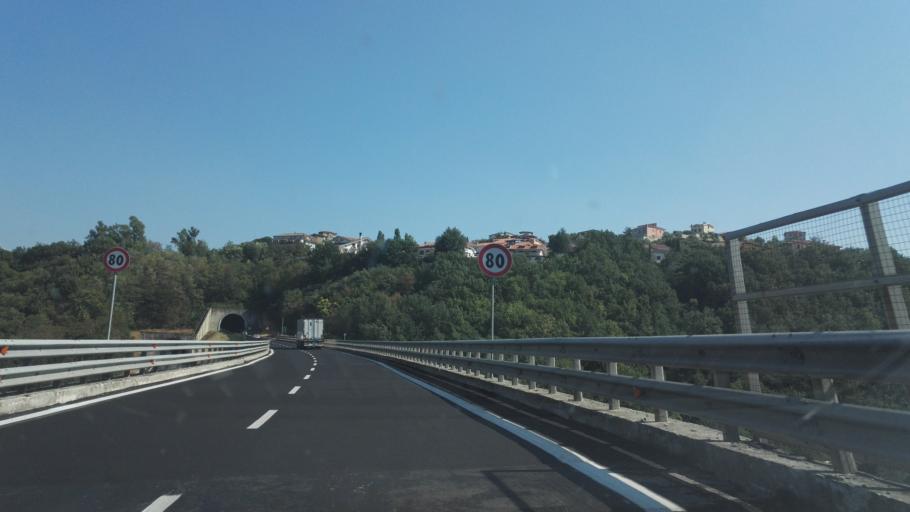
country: IT
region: Calabria
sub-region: Provincia di Cosenza
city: Rosario
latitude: 39.2884
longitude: 16.2395
